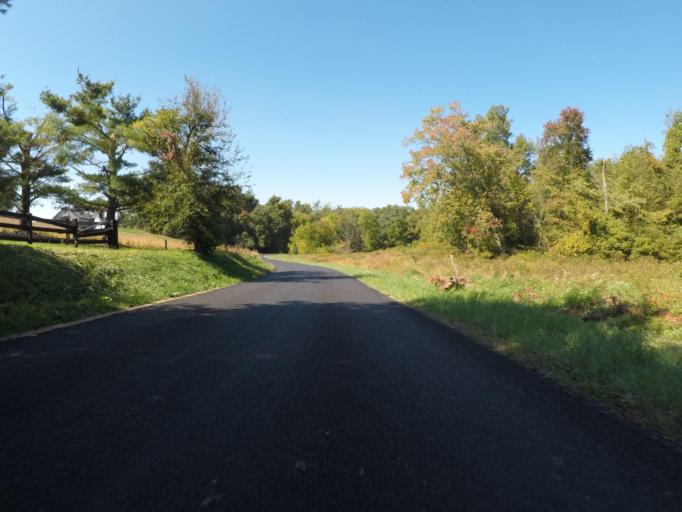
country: US
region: Maryland
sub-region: Carroll County
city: Hampstead
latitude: 39.5892
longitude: -76.8747
